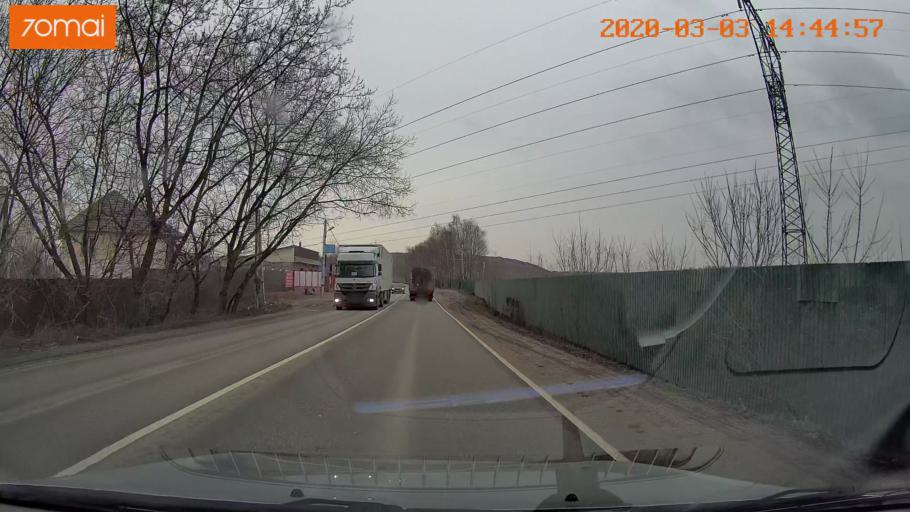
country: RU
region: Moskovskaya
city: Korenevo
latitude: 55.7013
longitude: 38.0386
